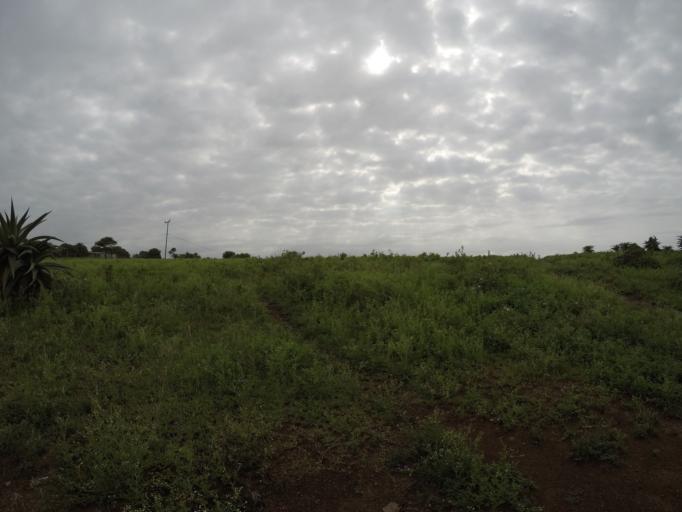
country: ZA
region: KwaZulu-Natal
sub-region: uThungulu District Municipality
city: Empangeni
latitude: -28.6395
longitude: 31.9059
